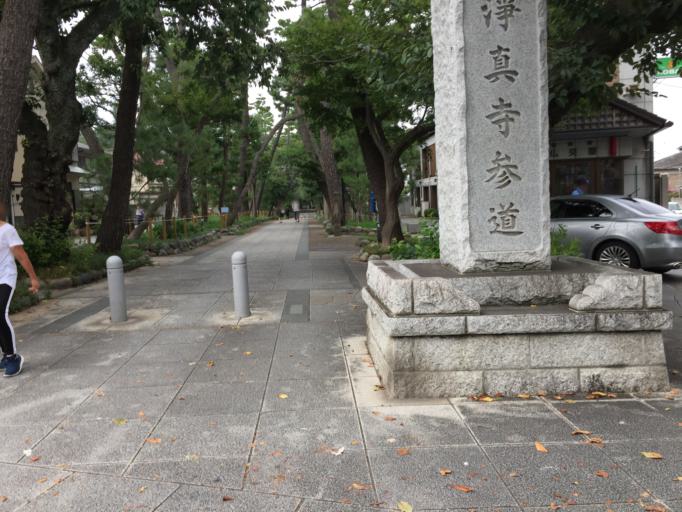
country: JP
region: Tokyo
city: Tokyo
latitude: 35.6057
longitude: 139.6618
